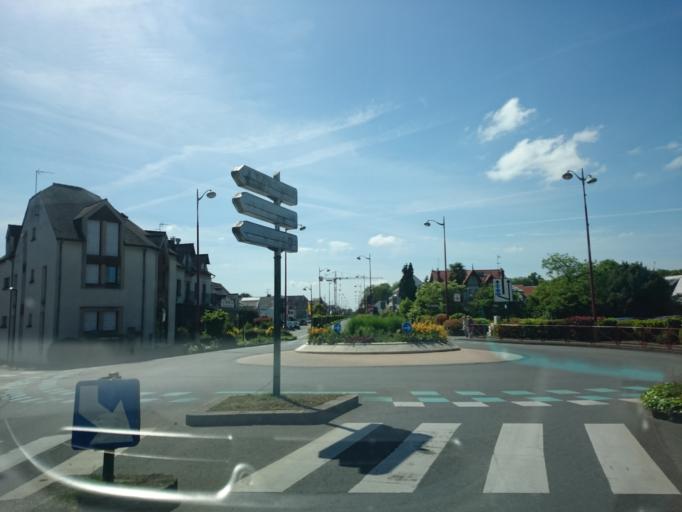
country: FR
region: Brittany
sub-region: Departement d'Ille-et-Vilaine
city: Cesson-Sevigne
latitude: 48.1143
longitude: -1.6099
